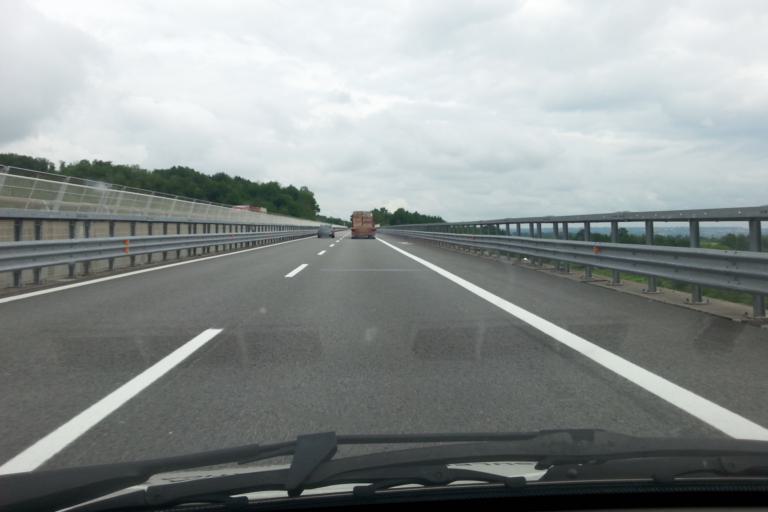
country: IT
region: Piedmont
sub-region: Provincia di Cuneo
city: Niella Tanaro
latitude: 44.4095
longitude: 7.9142
